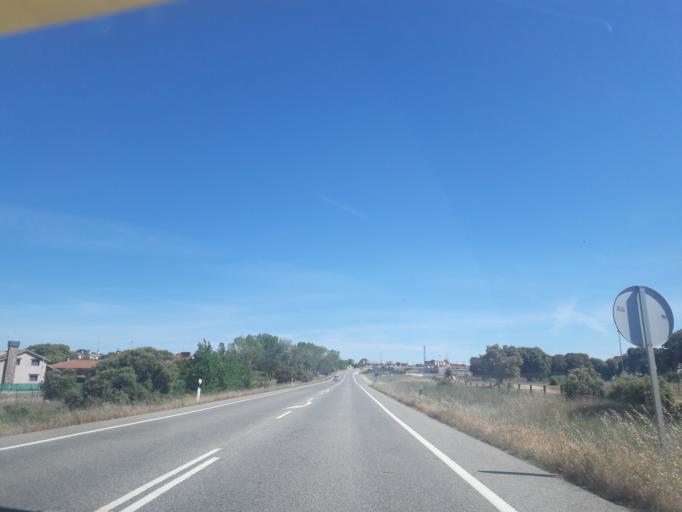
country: ES
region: Castille and Leon
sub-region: Provincia de Salamanca
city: Martinamor
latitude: 40.8035
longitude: -5.6329
